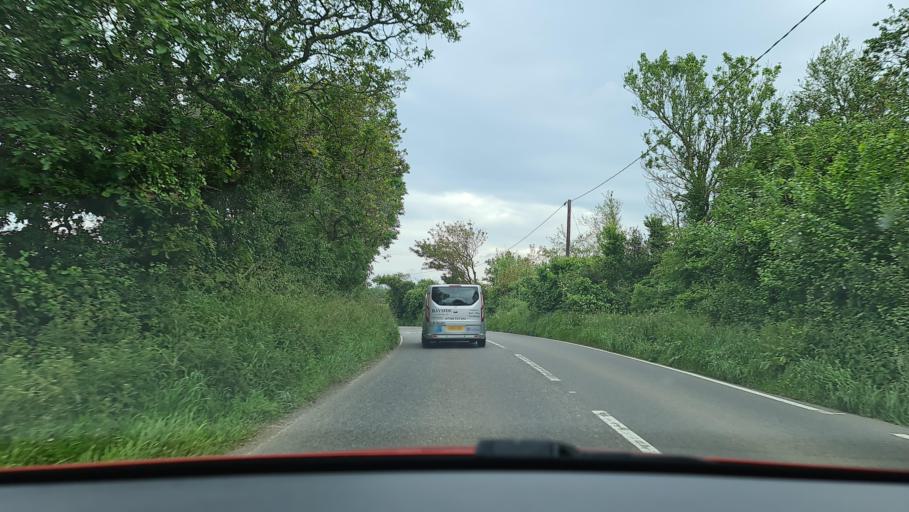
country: GB
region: England
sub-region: Cornwall
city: Poundstock
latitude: 50.7879
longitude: -4.5342
